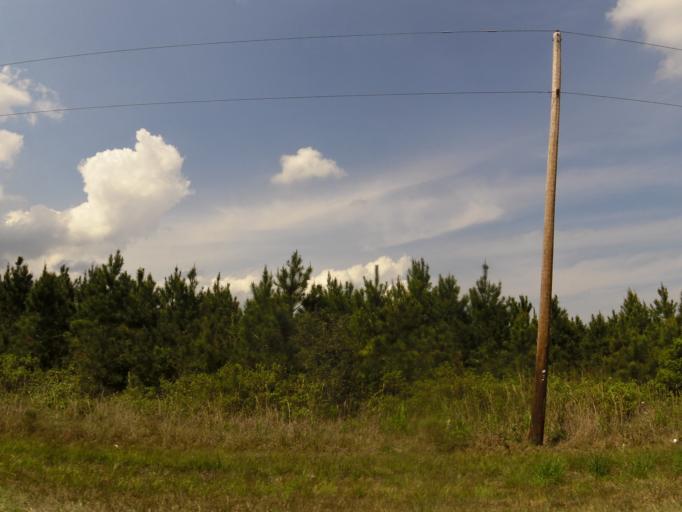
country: US
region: Georgia
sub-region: Camden County
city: Kingsland
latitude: 30.8109
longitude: -81.7662
